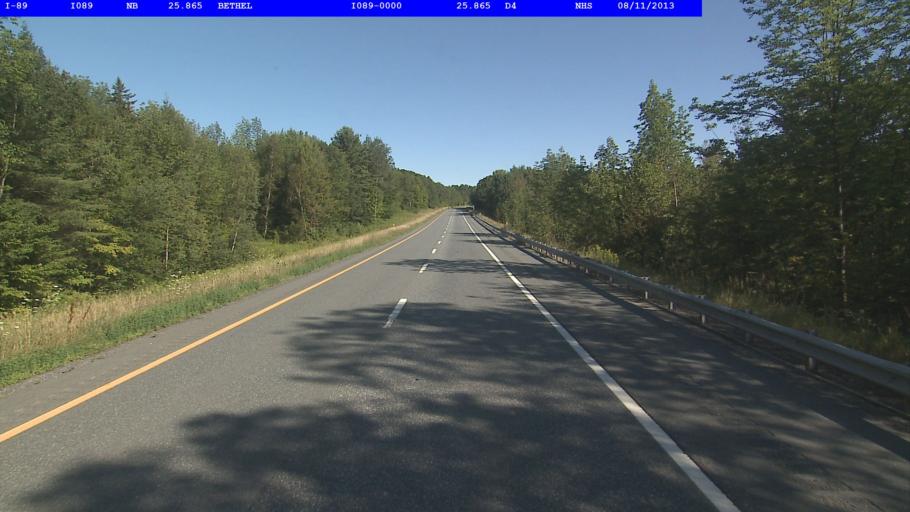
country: US
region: Vermont
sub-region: Orange County
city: Randolph
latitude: 43.8733
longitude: -72.6122
